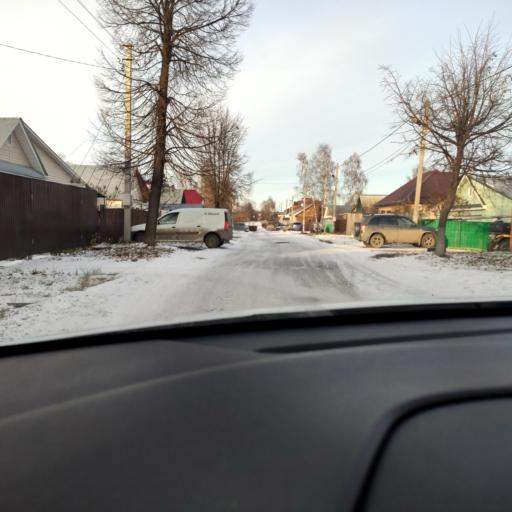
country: RU
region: Tatarstan
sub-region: Gorod Kazan'
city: Kazan
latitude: 55.8727
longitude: 49.0668
